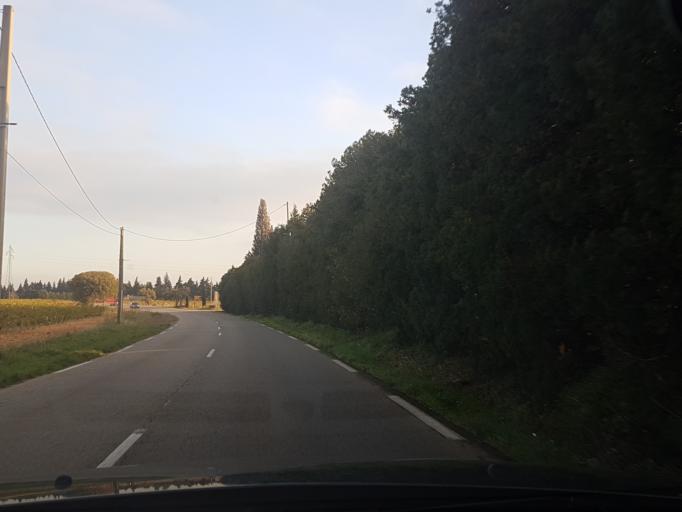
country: FR
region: Provence-Alpes-Cote d'Azur
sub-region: Departement du Vaucluse
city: Sorgues
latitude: 44.0333
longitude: 4.8585
